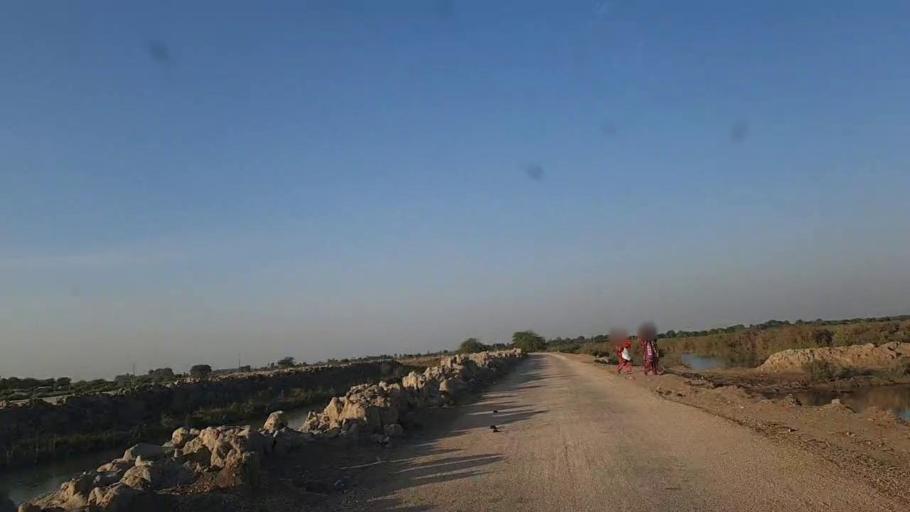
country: PK
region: Sindh
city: Mirpur Batoro
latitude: 24.6949
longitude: 68.2004
